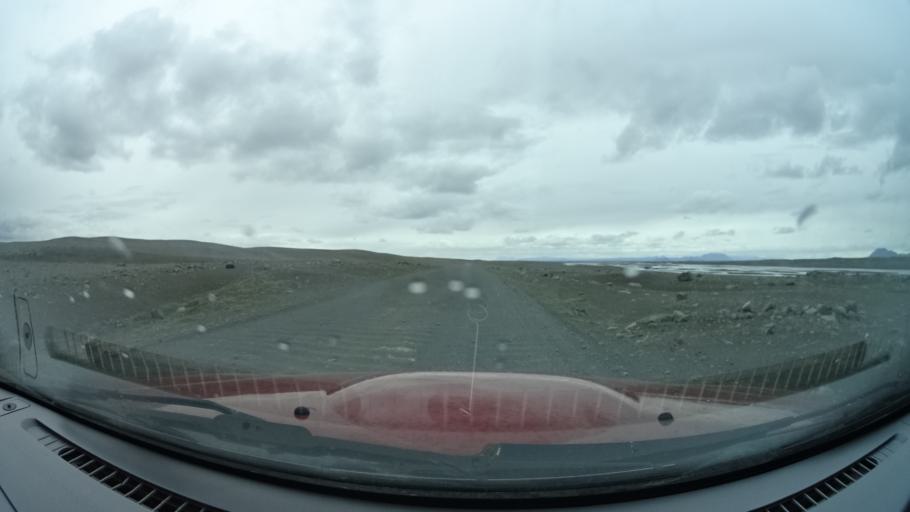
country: IS
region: Northeast
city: Husavik
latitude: 65.7730
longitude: -16.3465
